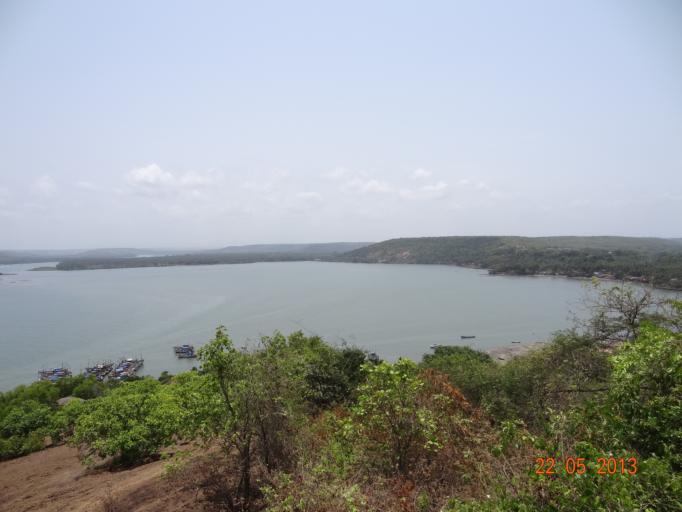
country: IN
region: Goa
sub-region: North Goa
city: Vagator
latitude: 15.6067
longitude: 73.7373
